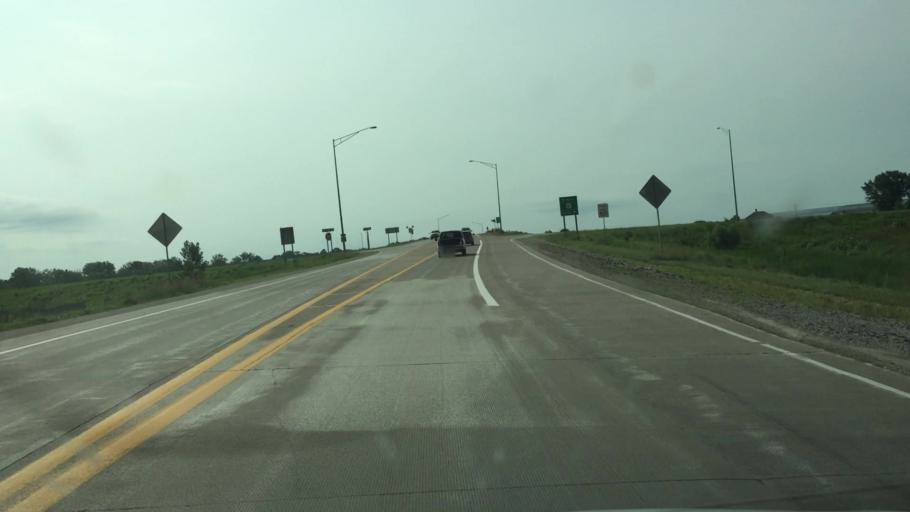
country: US
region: Illinois
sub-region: Hancock County
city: Nauvoo
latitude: 40.6282
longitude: -91.4016
